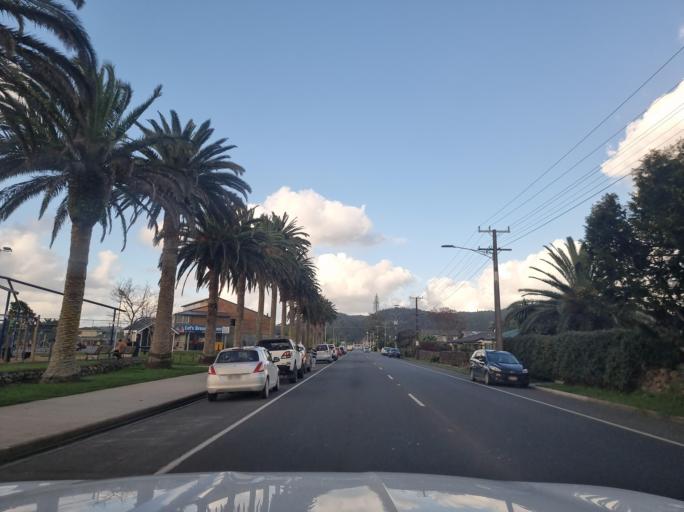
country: NZ
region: Northland
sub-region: Whangarei
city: Whangarei
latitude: -35.7097
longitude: 174.3158
